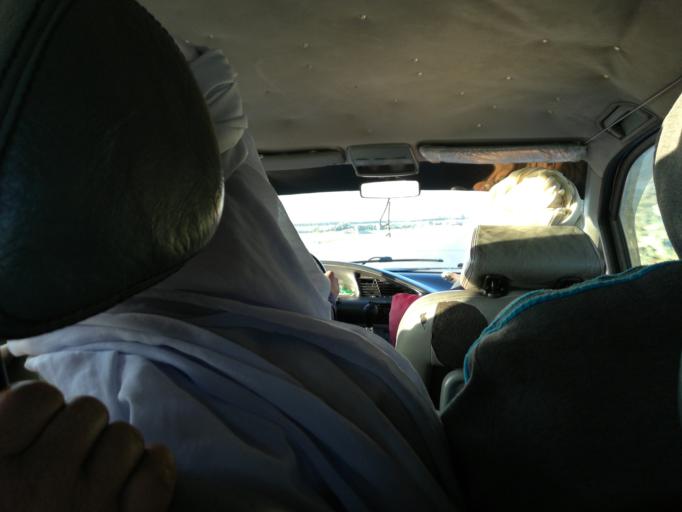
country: TN
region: Susah
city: Sidi Bou Ali
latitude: 36.0450
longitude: 10.3300
